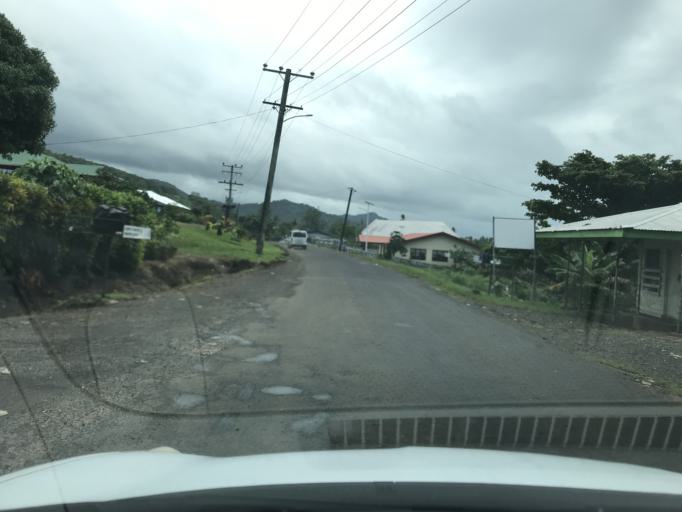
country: WS
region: Atua
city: Lufilufi
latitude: -13.8757
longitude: -171.6011
